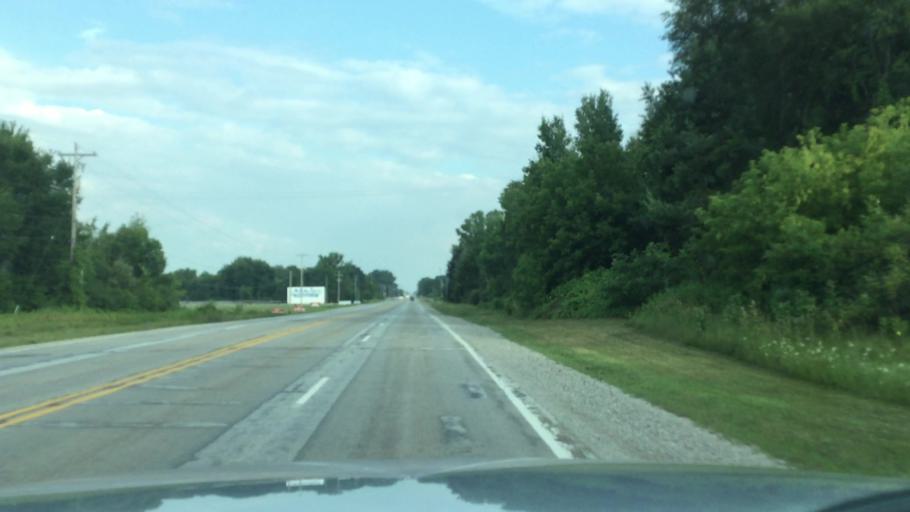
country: US
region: Michigan
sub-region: Saginaw County
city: Birch Run
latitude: 43.2685
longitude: -83.7832
